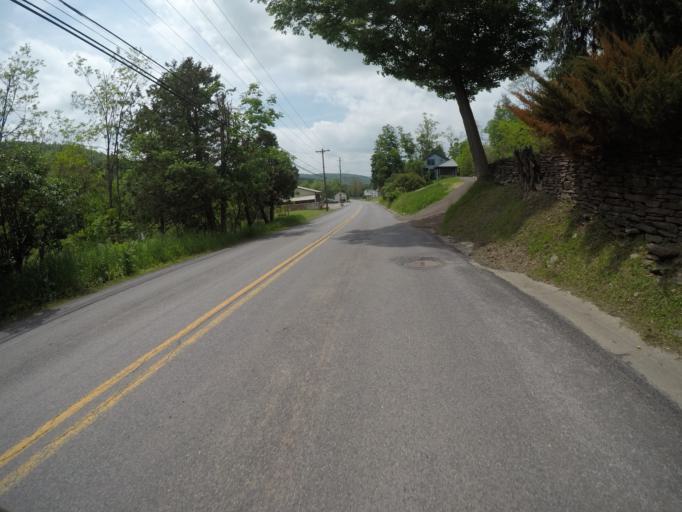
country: US
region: New York
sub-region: Delaware County
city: Delhi
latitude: 42.2612
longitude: -74.7892
